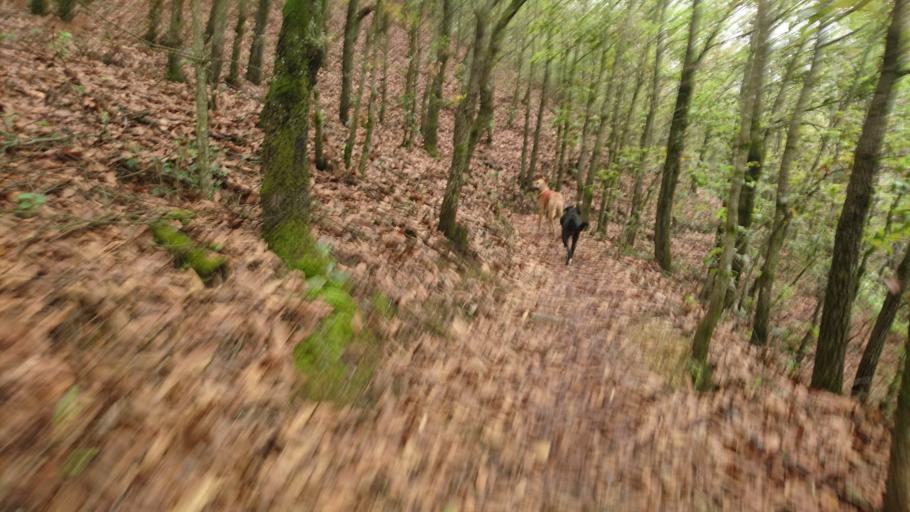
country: MX
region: Nuevo Leon
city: Garza Garcia
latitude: 25.6002
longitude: -100.3351
